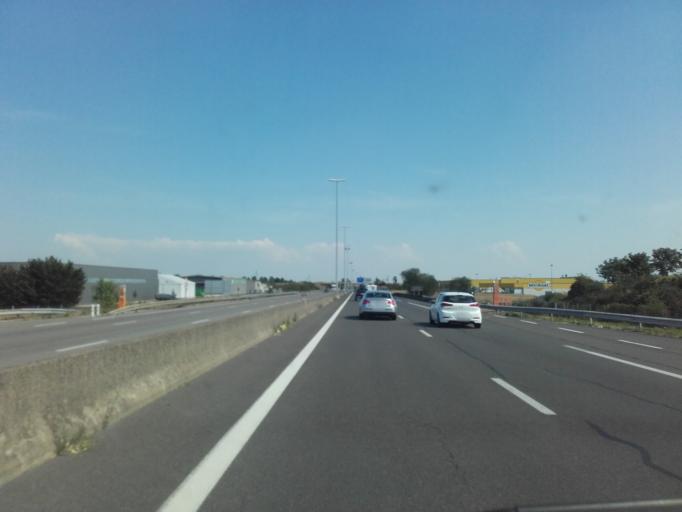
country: FR
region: Bourgogne
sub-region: Departement de la Cote-d'Or
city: Beaune
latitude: 47.0436
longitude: 4.8427
